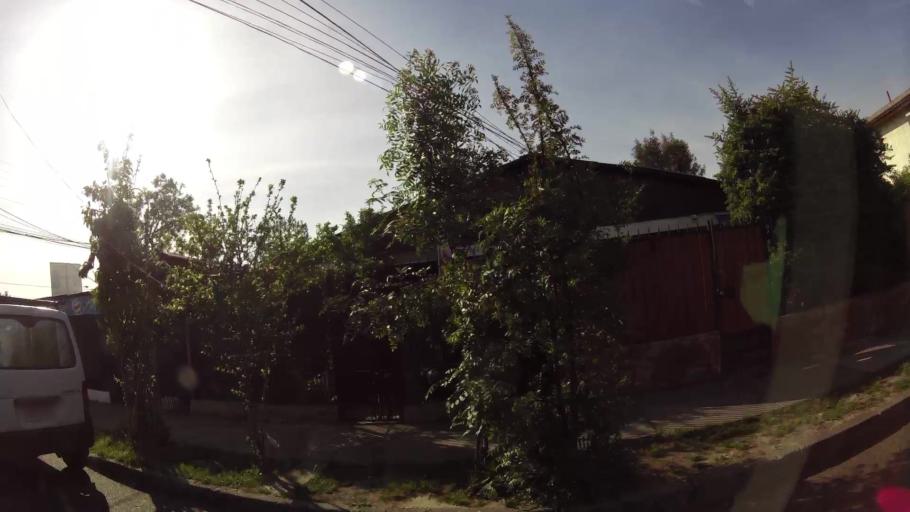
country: CL
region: Santiago Metropolitan
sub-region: Provincia de Santiago
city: Villa Presidente Frei, Nunoa, Santiago, Chile
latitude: -33.5342
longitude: -70.5776
